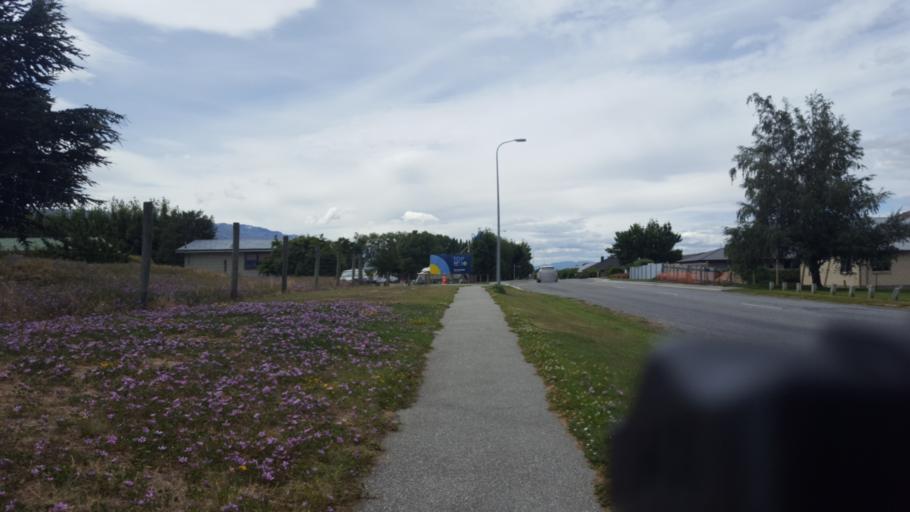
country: NZ
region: Otago
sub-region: Queenstown-Lakes District
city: Wanaka
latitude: -45.0409
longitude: 169.2145
